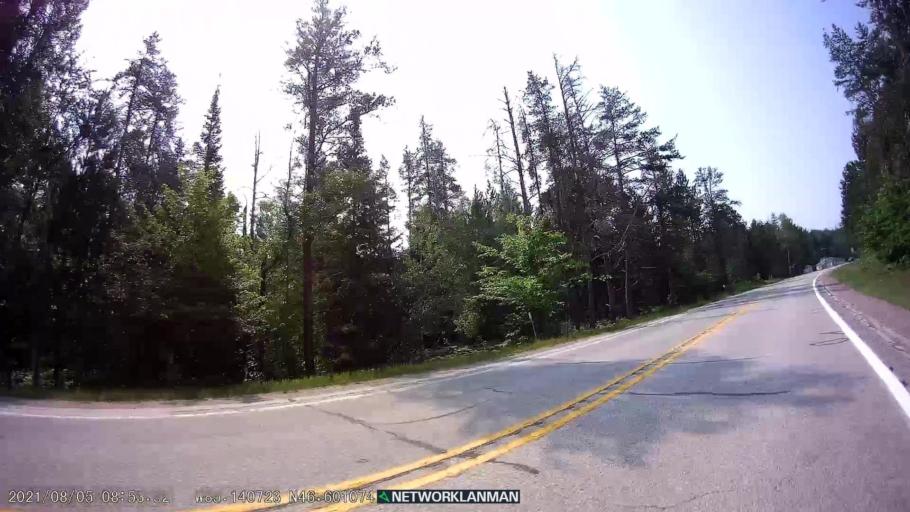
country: US
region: Michigan
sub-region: Luce County
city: Newberry
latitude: 46.6006
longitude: -85.1412
